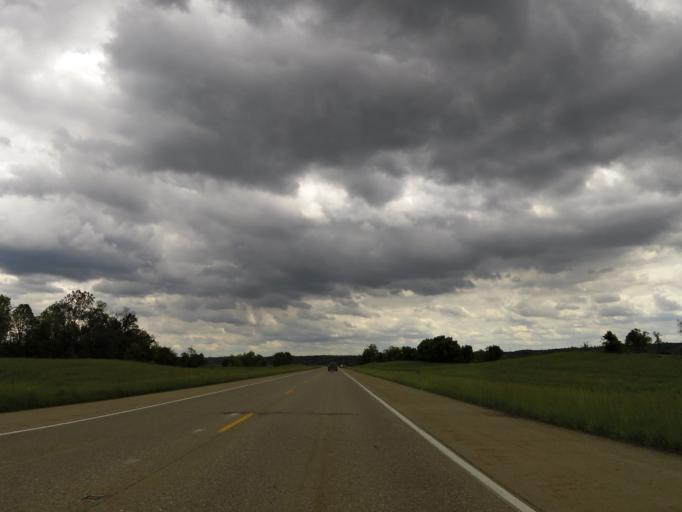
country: US
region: West Virginia
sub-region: Jackson County
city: Ravenswood
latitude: 38.9400
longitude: -81.7899
